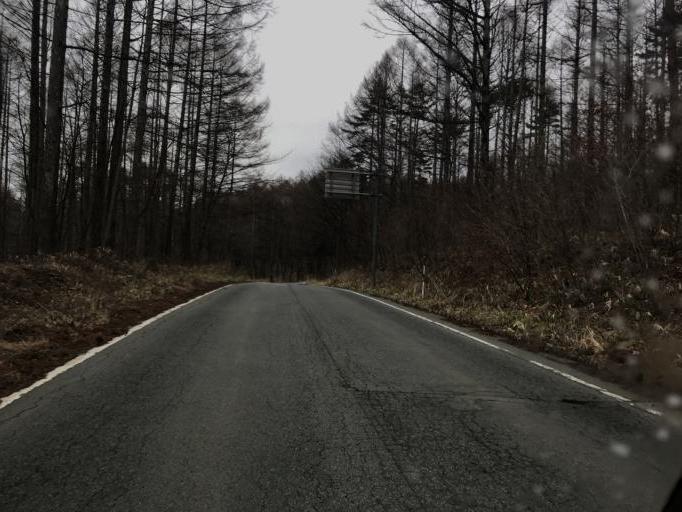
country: JP
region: Nagano
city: Chino
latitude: 35.8957
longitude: 138.3233
